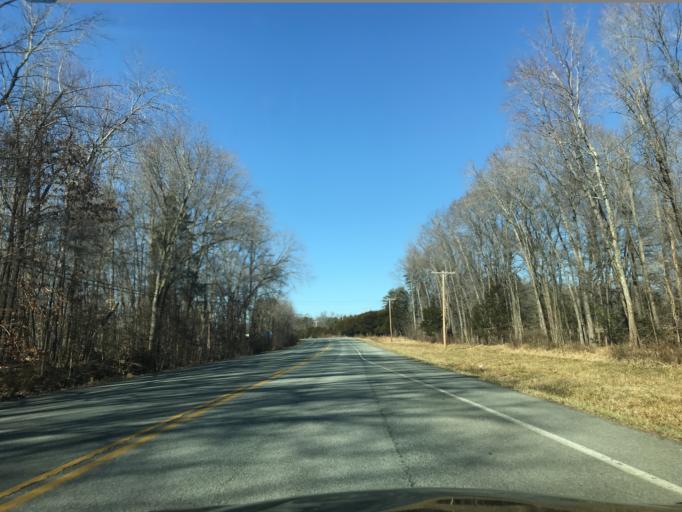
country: US
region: Maryland
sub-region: Charles County
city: Bryans Road
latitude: 38.6599
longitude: -77.0789
